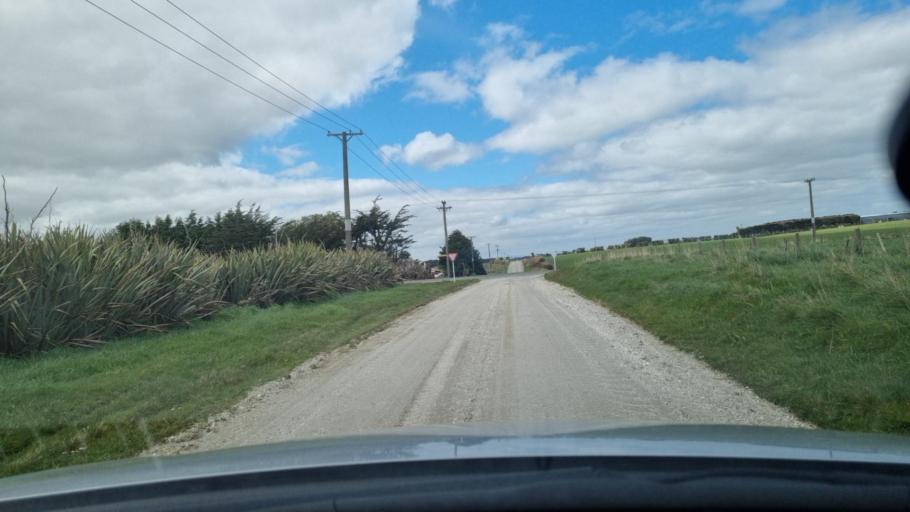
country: NZ
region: Southland
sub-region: Invercargill City
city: Invercargill
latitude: -46.4427
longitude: 168.4575
